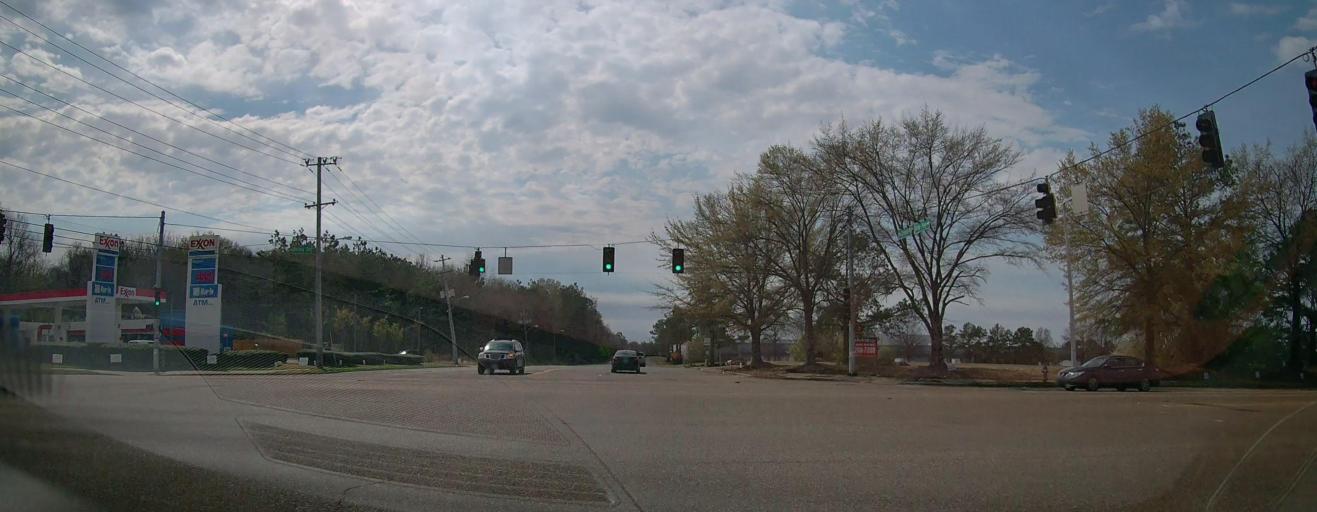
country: US
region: Mississippi
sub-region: De Soto County
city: Olive Branch
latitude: 35.0205
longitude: -89.8487
